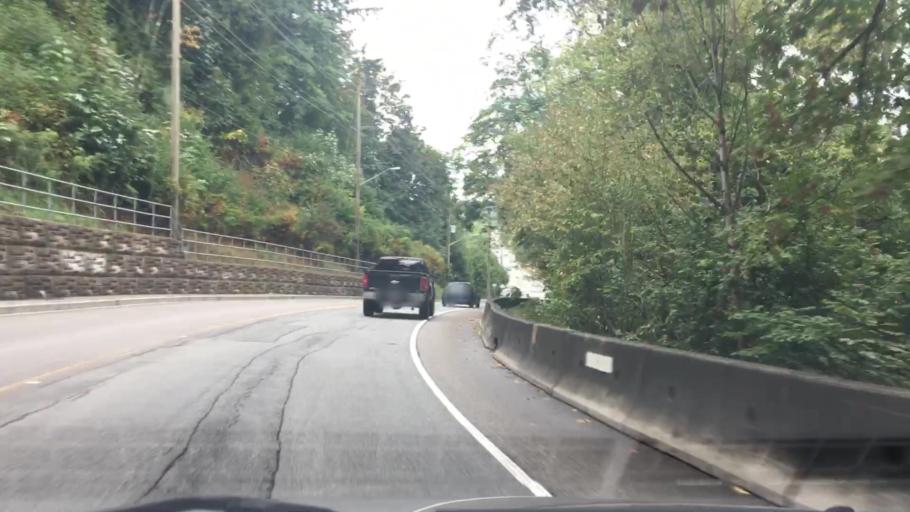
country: CA
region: British Columbia
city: Langley
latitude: 49.1039
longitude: -122.5700
